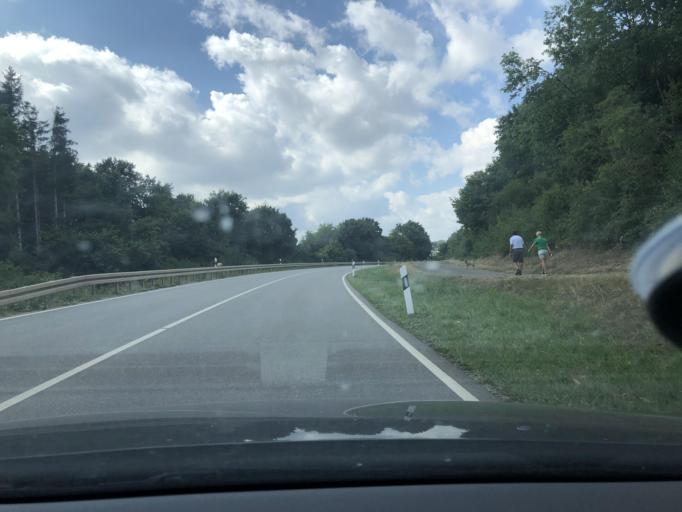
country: DE
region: Baden-Wuerttemberg
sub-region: Tuebingen Region
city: Pfullingen
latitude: 48.4147
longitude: 9.2085
